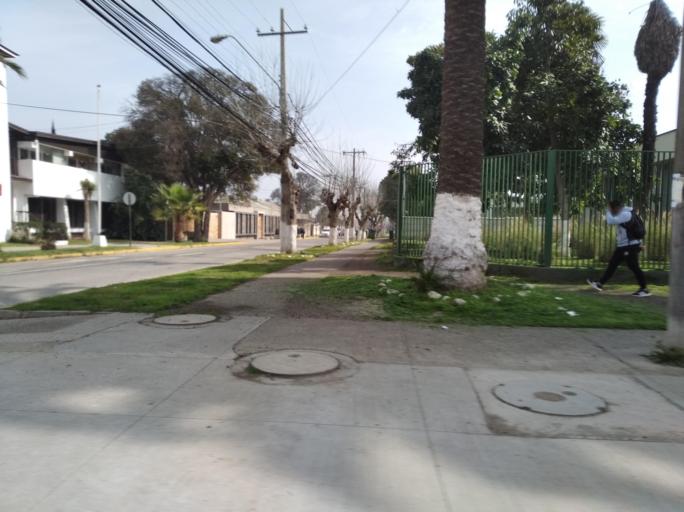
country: CL
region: Valparaiso
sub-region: Provincia de Marga Marga
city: Limache
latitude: -32.9867
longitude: -71.2786
